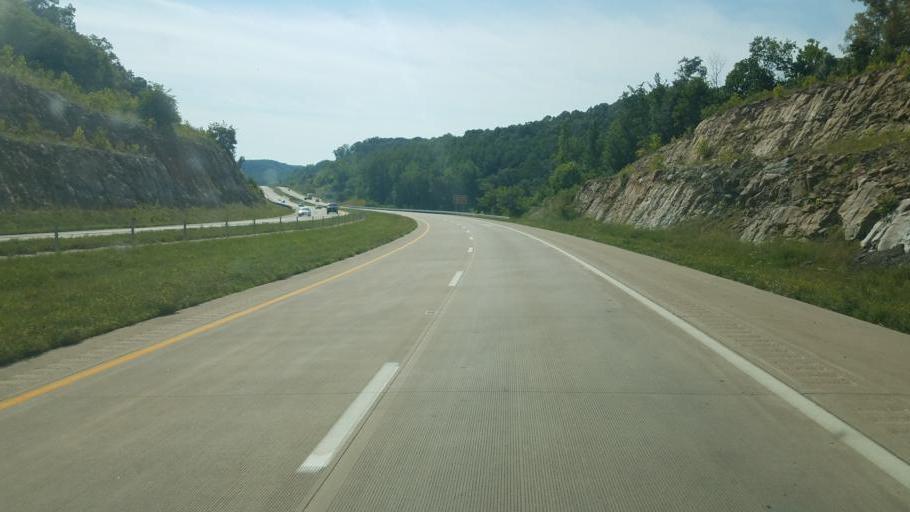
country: US
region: Ohio
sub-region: Athens County
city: Nelsonville
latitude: 39.4722
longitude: -82.2318
